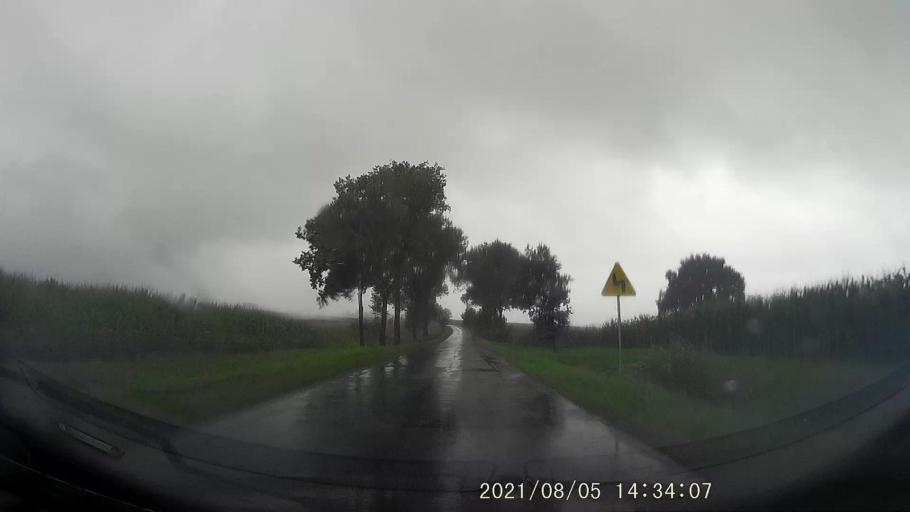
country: PL
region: Opole Voivodeship
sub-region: Powiat nyski
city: Korfantow
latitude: 50.4683
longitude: 17.5244
